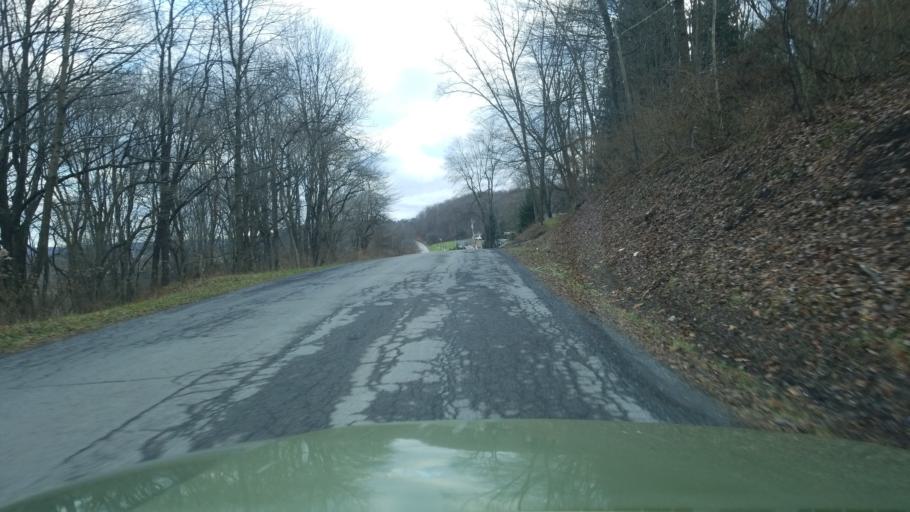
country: US
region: Pennsylvania
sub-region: Jefferson County
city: Falls Creek
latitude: 41.1345
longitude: -78.7866
